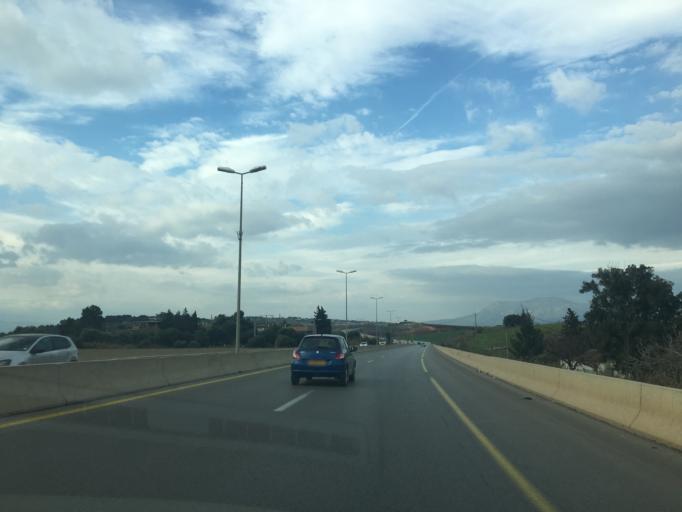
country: DZ
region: Tipaza
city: Tipasa
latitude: 36.5759
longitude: 2.5388
